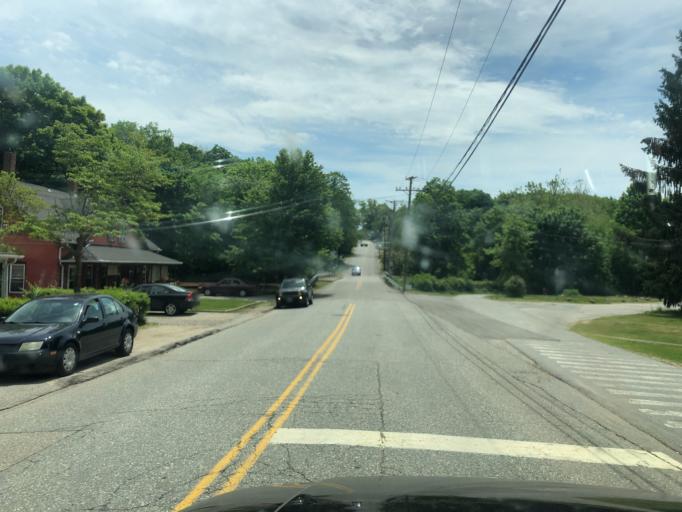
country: US
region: Connecticut
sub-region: Windham County
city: North Grosvenor Dale
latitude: 41.9886
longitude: -71.8957
